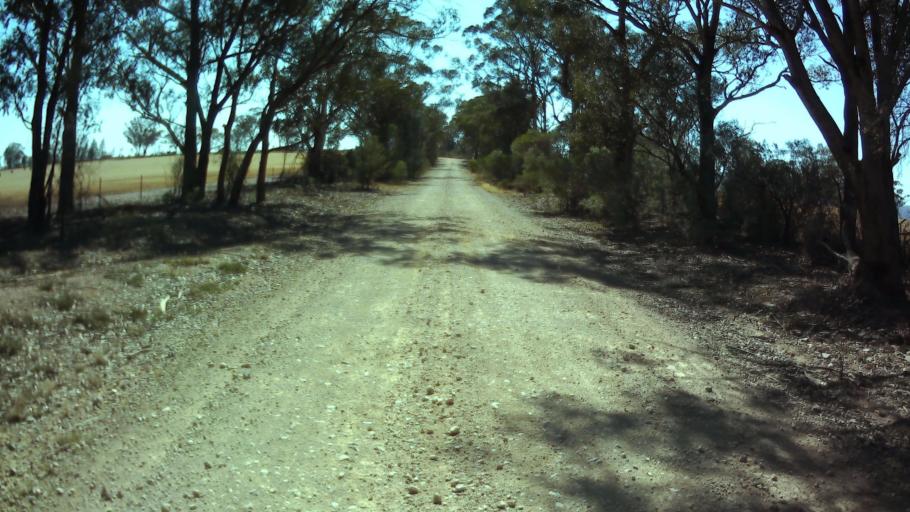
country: AU
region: New South Wales
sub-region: Weddin
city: Grenfell
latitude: -33.9017
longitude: 147.8751
